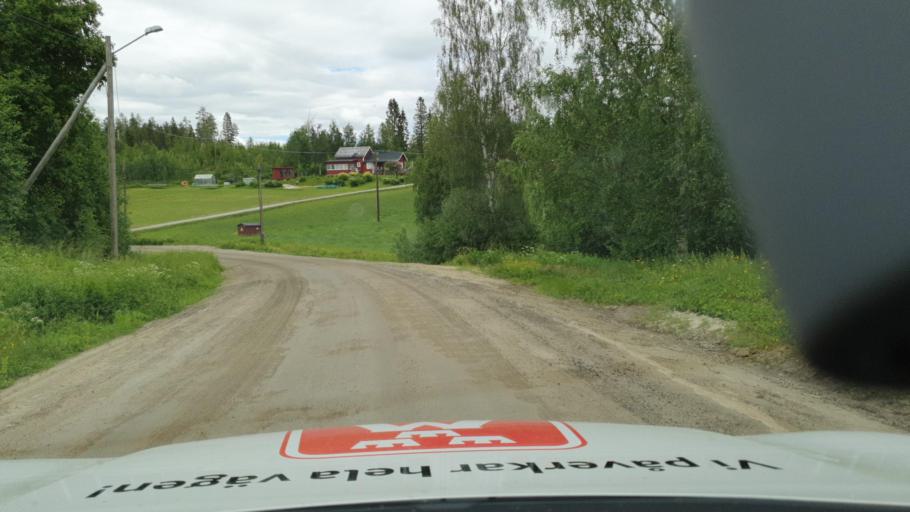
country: SE
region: Vaesterbotten
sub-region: Nordmalings Kommun
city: Nordmaling
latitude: 63.6811
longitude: 19.4526
